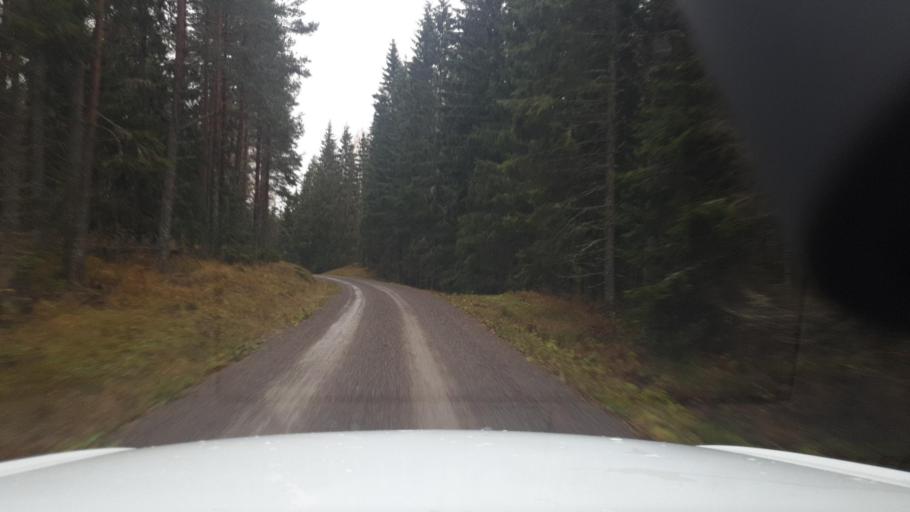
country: SE
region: Vaermland
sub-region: Eda Kommun
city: Charlottenberg
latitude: 60.0320
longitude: 12.6318
